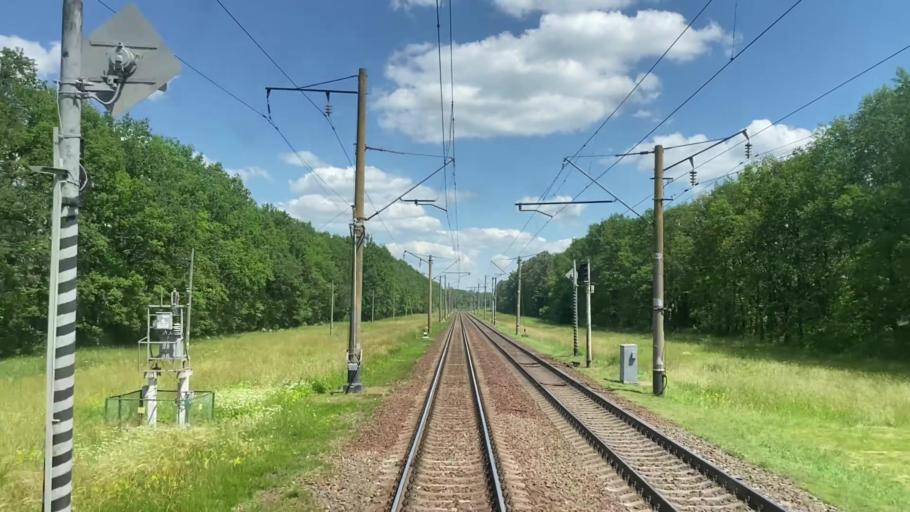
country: BY
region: Brest
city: Pruzhany
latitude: 52.4988
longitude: 24.6144
